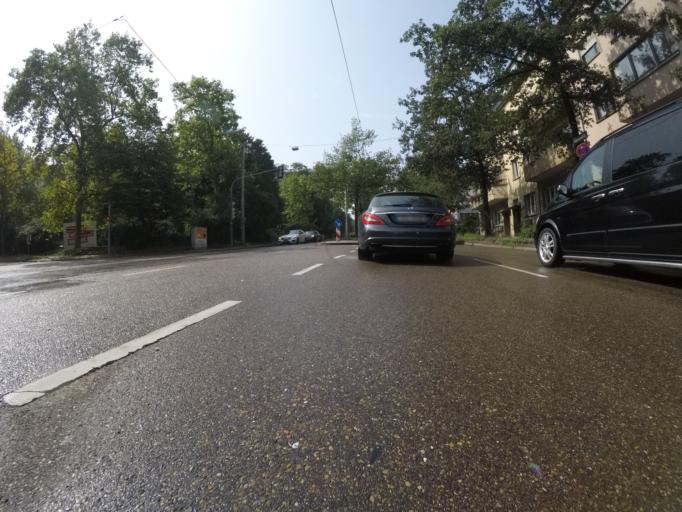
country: DE
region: Baden-Wuerttemberg
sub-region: Regierungsbezirk Stuttgart
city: Stuttgart
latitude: 48.7714
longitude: 9.1450
